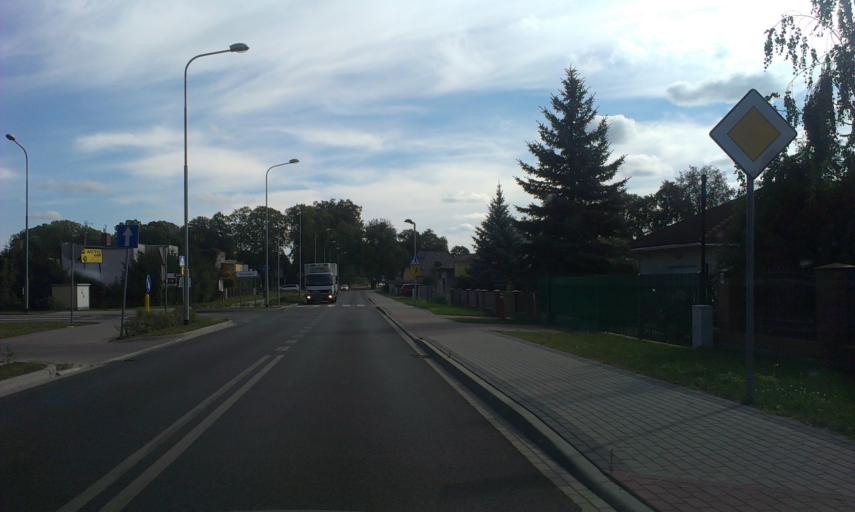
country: PL
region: Greater Poland Voivodeship
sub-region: Powiat zlotowski
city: Zlotow
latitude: 53.3689
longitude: 17.0246
